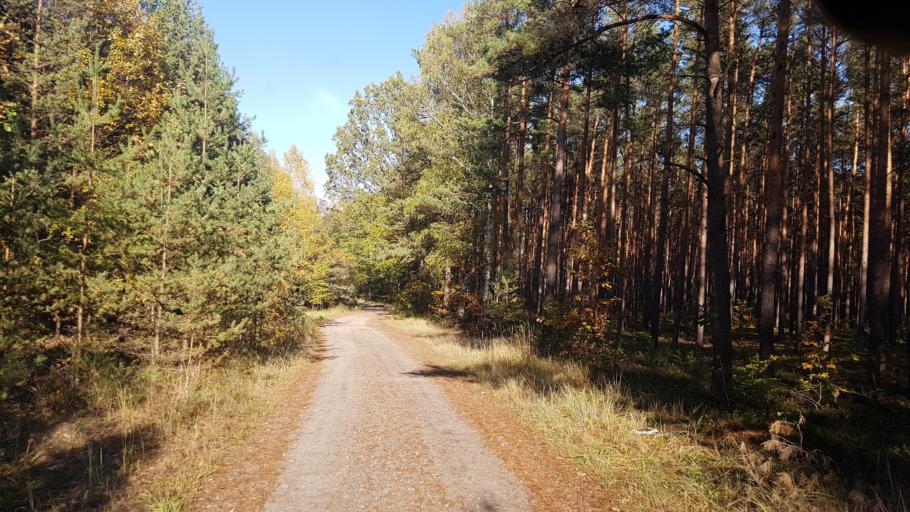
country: DE
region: Brandenburg
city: Ruckersdorf
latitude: 51.5483
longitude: 13.5363
